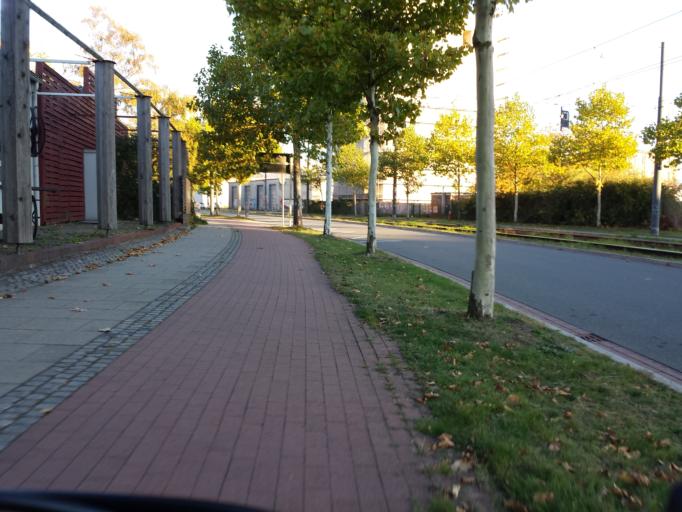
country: DE
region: Bremen
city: Bremen
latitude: 53.0838
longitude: 8.7812
